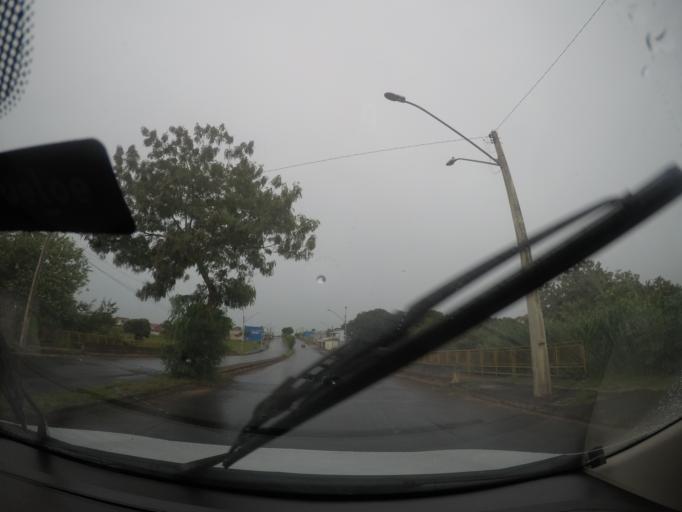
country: BR
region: Goias
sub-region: Goiania
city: Goiania
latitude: -16.6747
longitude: -49.3201
